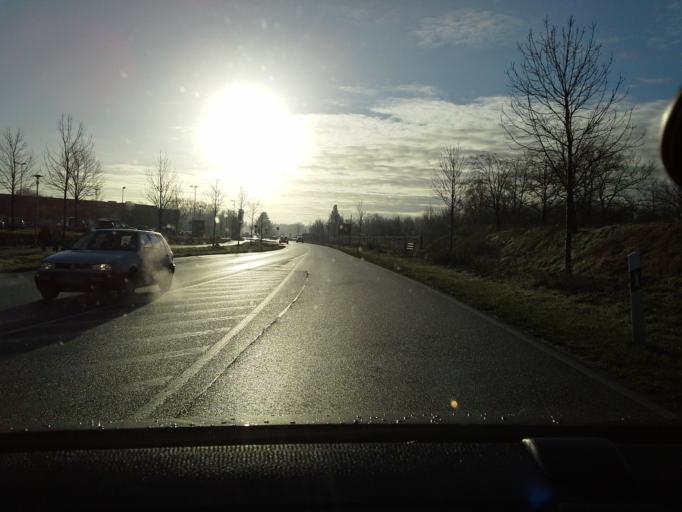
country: DE
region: Schleswig-Holstein
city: Pinneberg
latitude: 53.6469
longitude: 9.7689
